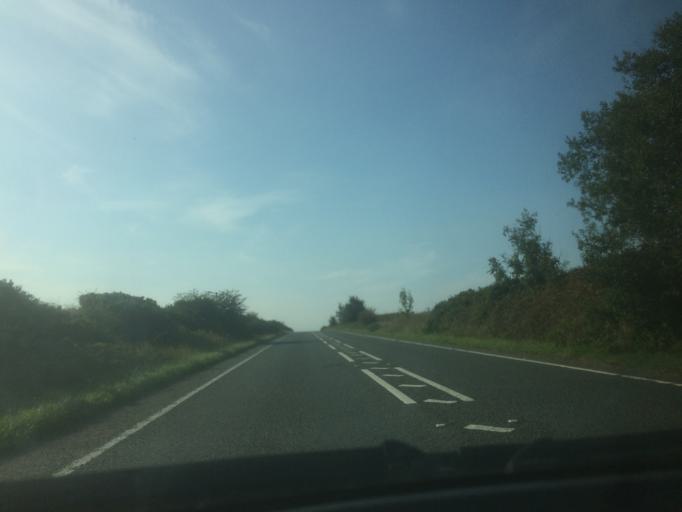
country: GB
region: England
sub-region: Cornwall
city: Callington
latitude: 50.4860
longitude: -4.2870
